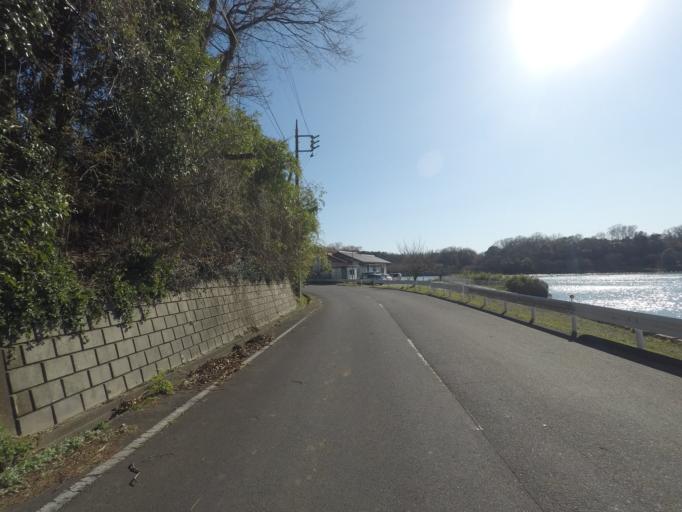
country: JP
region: Ibaraki
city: Makabe
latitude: 36.2402
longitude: 140.0728
